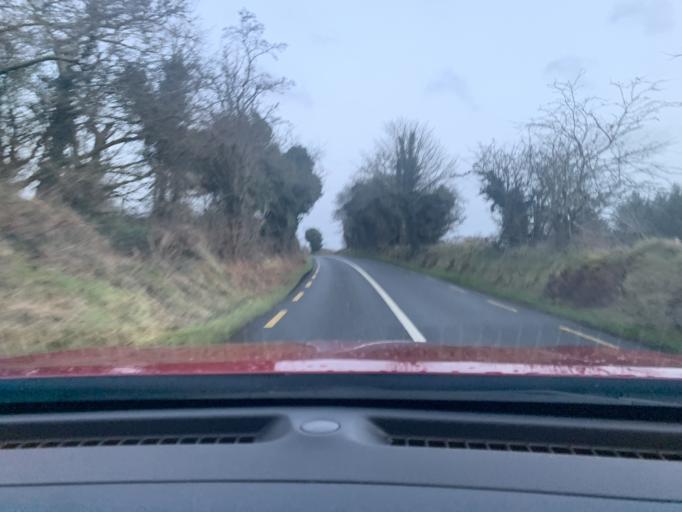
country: IE
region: Connaught
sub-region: Sligo
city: Ballymote
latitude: 54.0368
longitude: -8.4281
